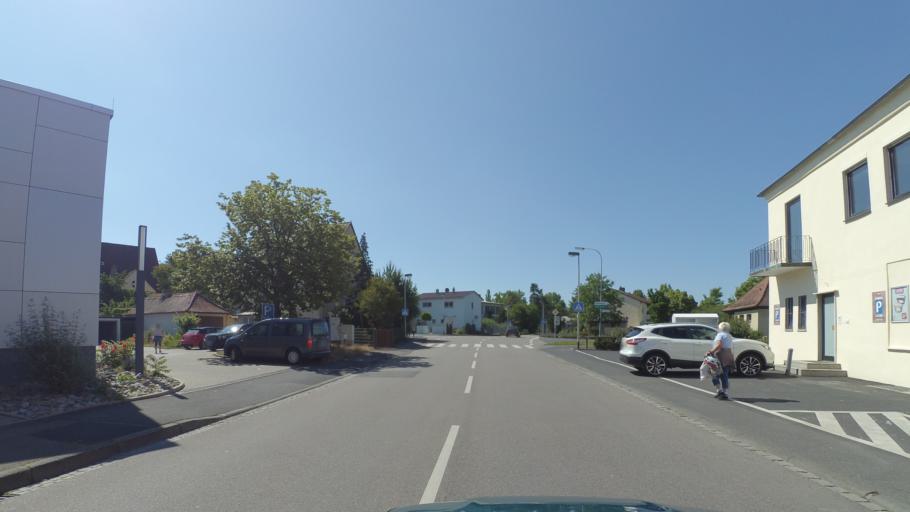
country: DE
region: Bavaria
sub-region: Regierungsbezirk Unterfranken
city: Kitzingen
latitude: 49.7305
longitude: 10.1815
